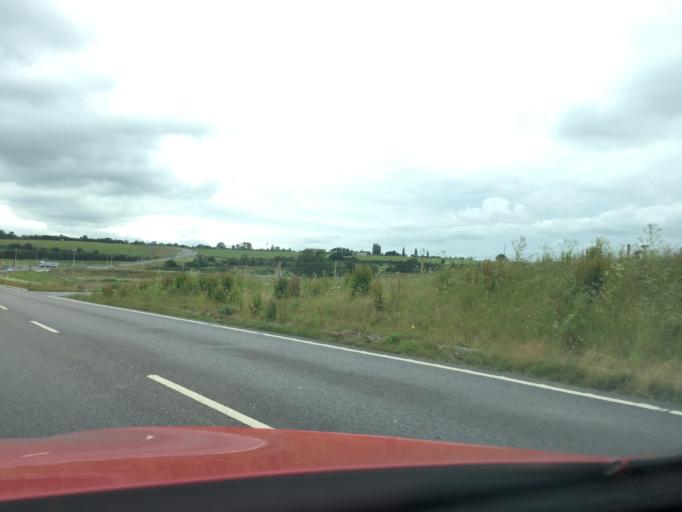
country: GB
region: England
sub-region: Northamptonshire
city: Long Buckby
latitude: 52.2408
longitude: -1.0769
